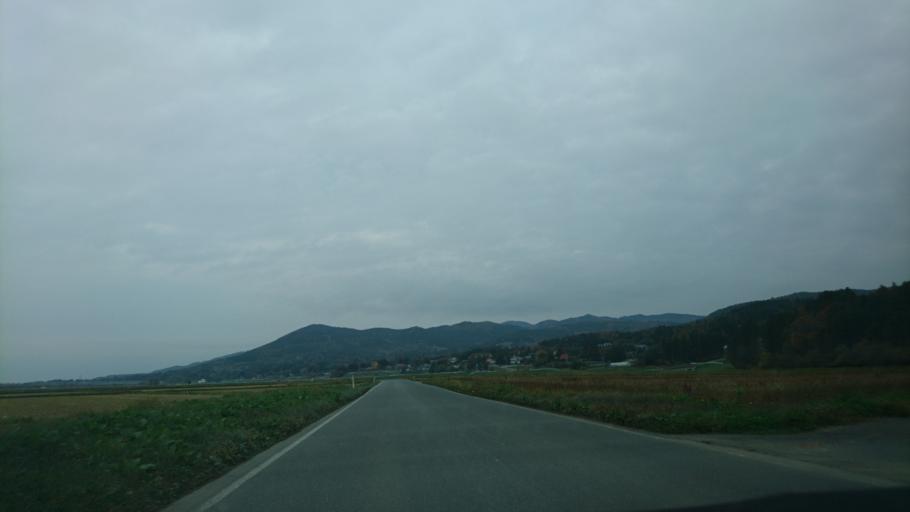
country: JP
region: Iwate
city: Ichinoseki
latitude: 38.9531
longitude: 141.1689
